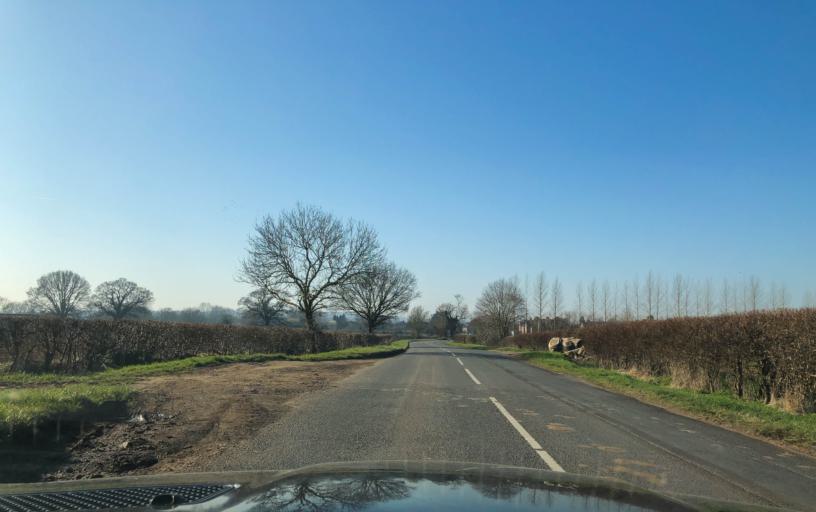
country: GB
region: England
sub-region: Warwickshire
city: Wellesbourne Mountford
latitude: 52.2019
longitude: -1.5846
